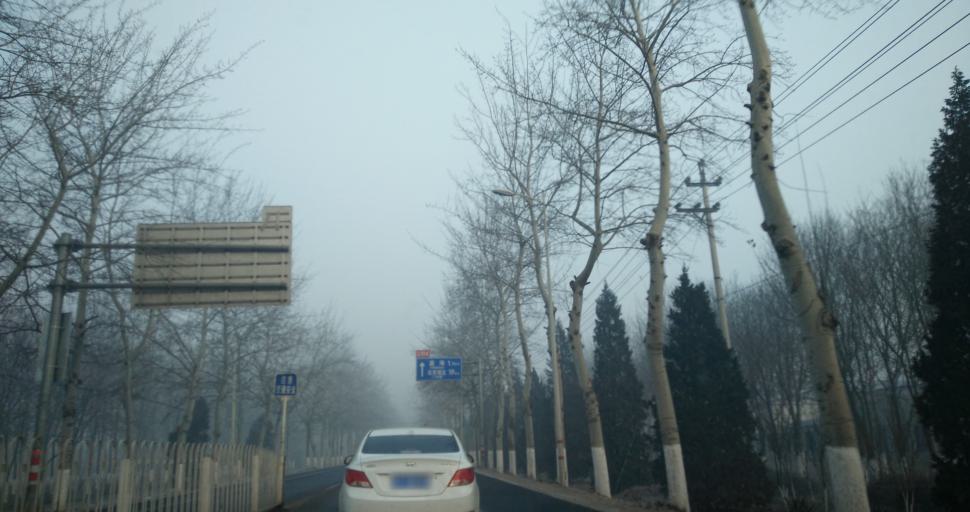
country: CN
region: Beijing
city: Yinghai
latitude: 39.7426
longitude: 116.4487
